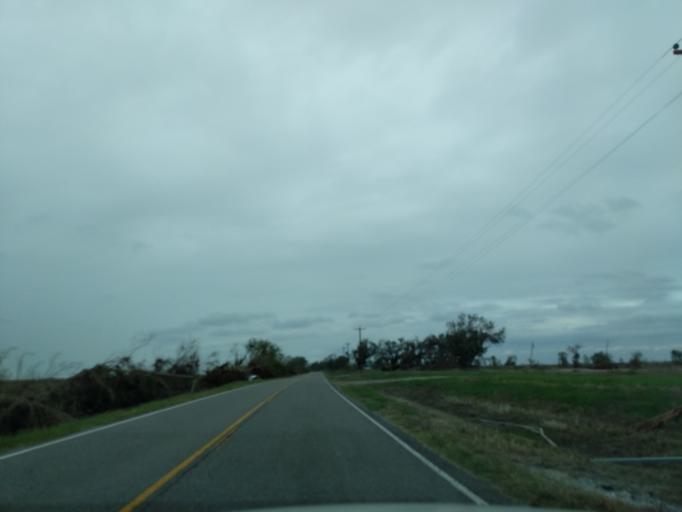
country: US
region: Louisiana
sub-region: Cameron Parish
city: Cameron
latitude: 29.7868
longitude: -93.1333
